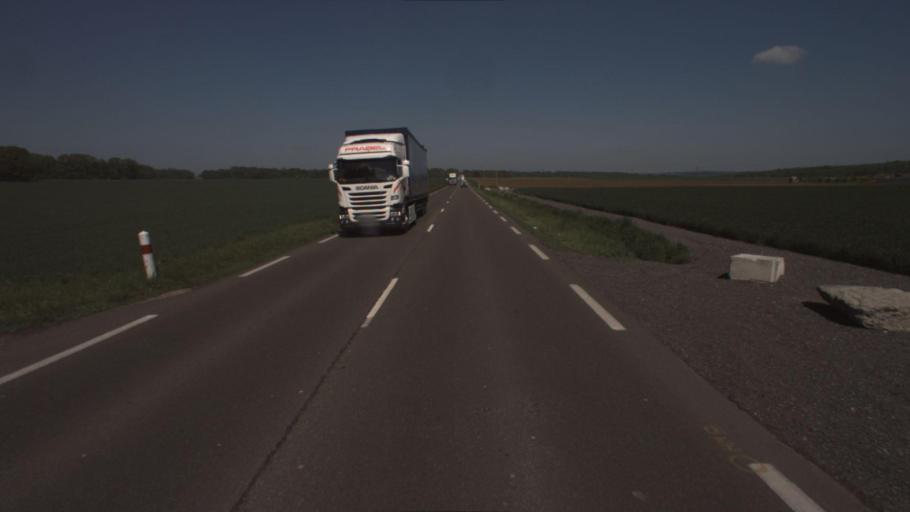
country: FR
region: Ile-de-France
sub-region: Departement de Seine-et-Marne
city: Voulangis
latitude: 48.8358
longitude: 2.8769
